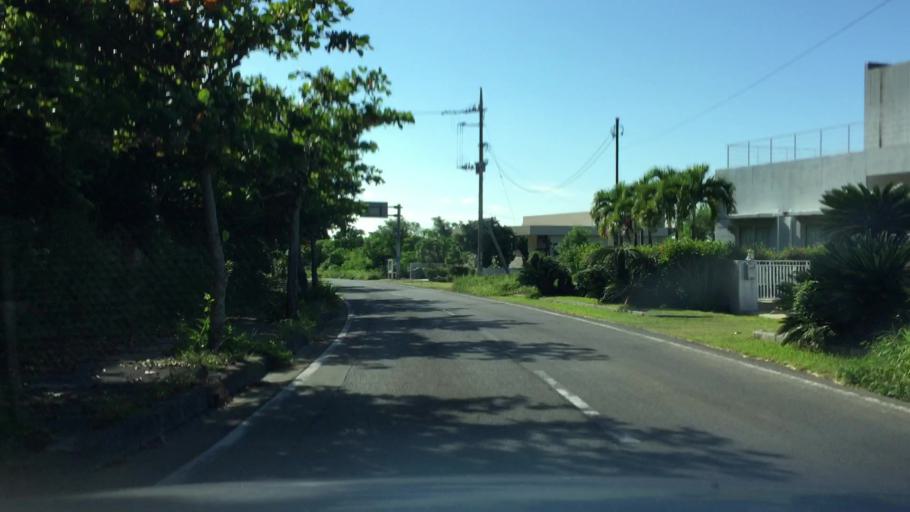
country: JP
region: Okinawa
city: Ishigaki
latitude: 24.4473
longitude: 124.1700
